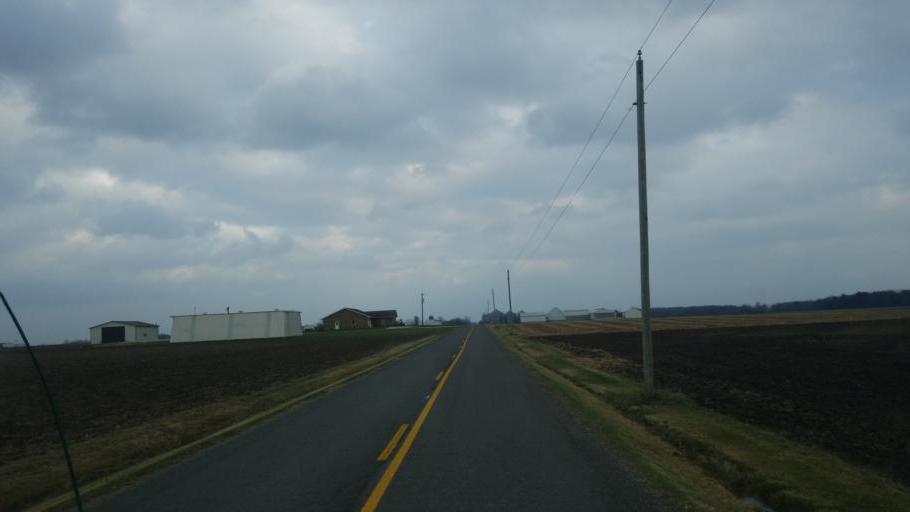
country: US
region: Ohio
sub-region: Mercer County
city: Fort Recovery
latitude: 40.5090
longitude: -84.7616
